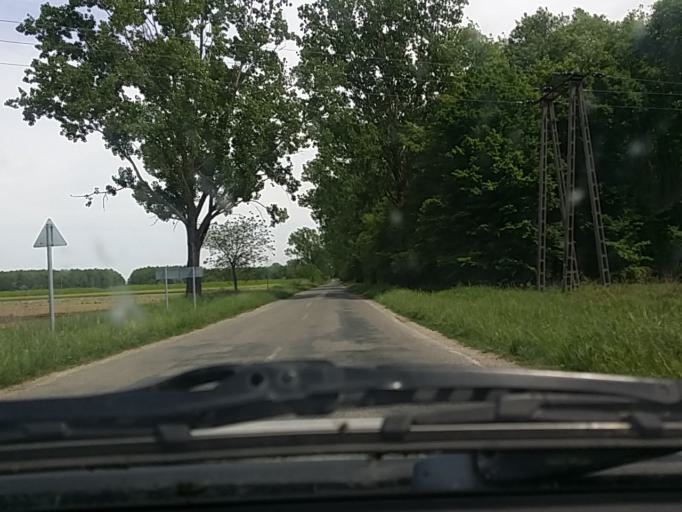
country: HU
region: Somogy
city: Barcs
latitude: 45.9542
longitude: 17.6040
